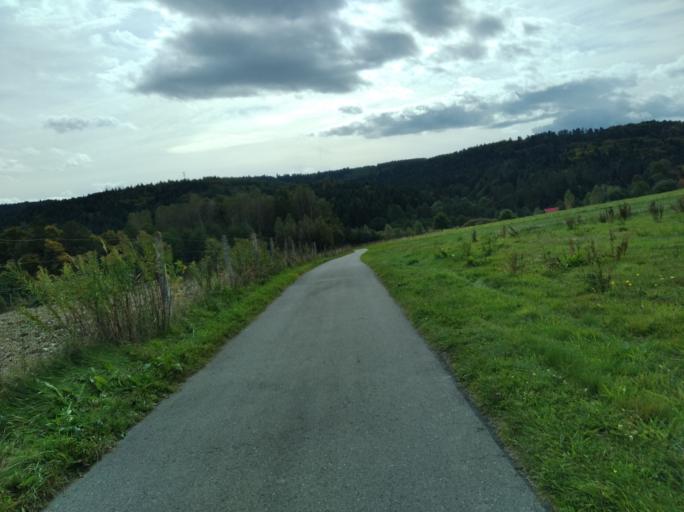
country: PL
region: Subcarpathian Voivodeship
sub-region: Powiat strzyzowski
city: Jawornik
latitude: 49.8360
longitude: 21.8934
